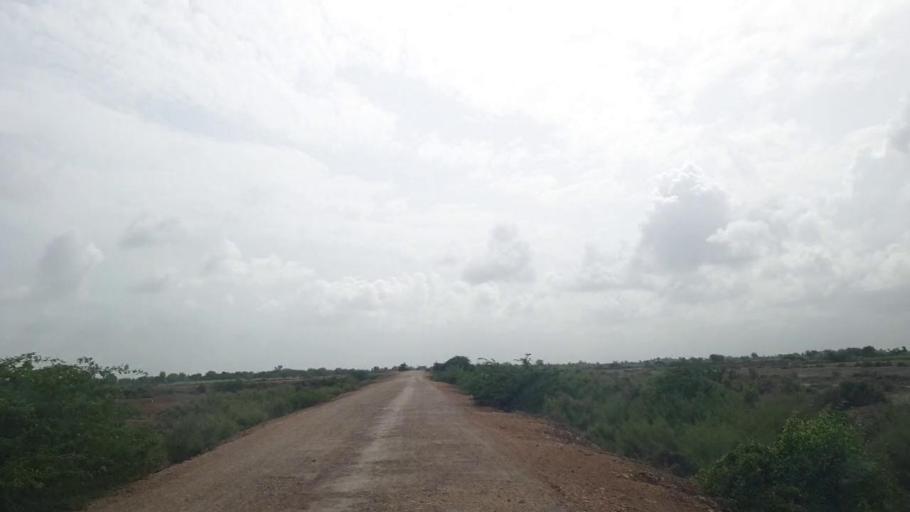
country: PK
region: Sindh
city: Tando Bago
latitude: 24.8242
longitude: 69.0647
